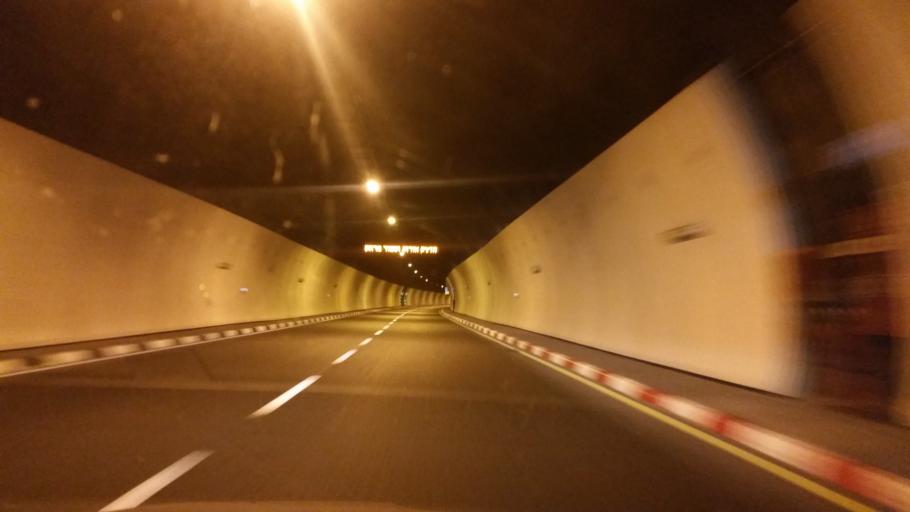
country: IL
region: Haifa
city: Haifa
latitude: 32.7923
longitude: 34.9715
